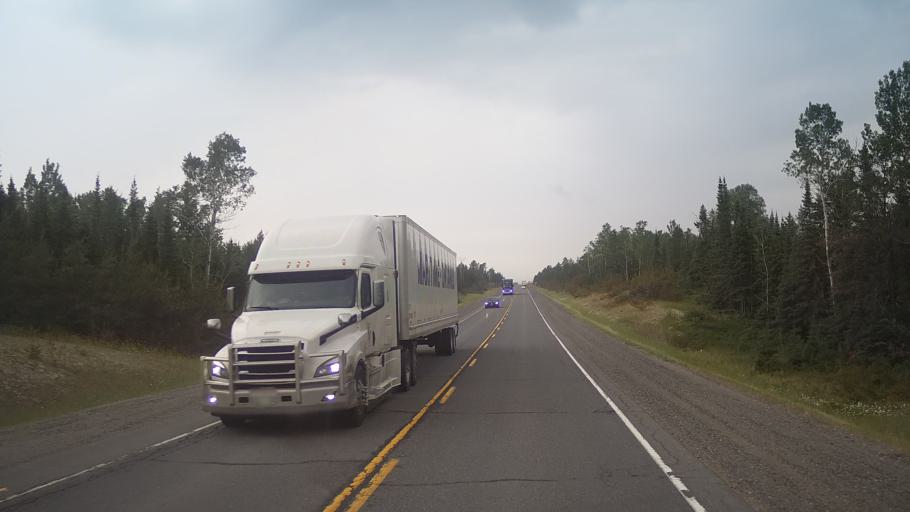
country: CA
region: Ontario
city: Greenstone
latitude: 49.2058
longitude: -88.2082
